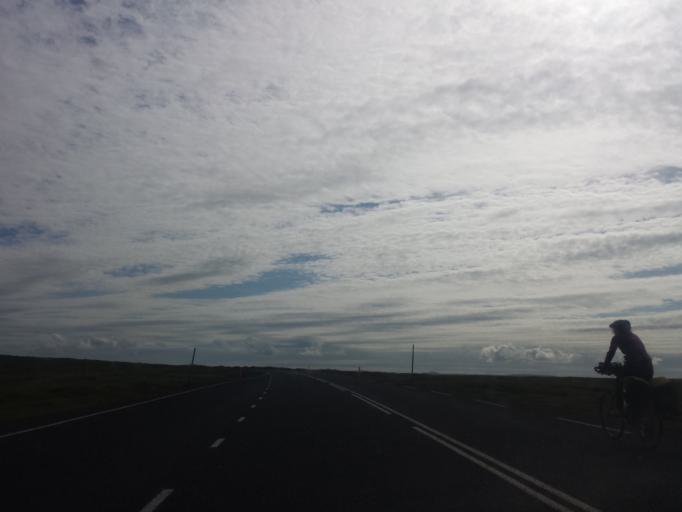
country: IS
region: Northeast
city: Husavik
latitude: 66.0208
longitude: -16.5714
